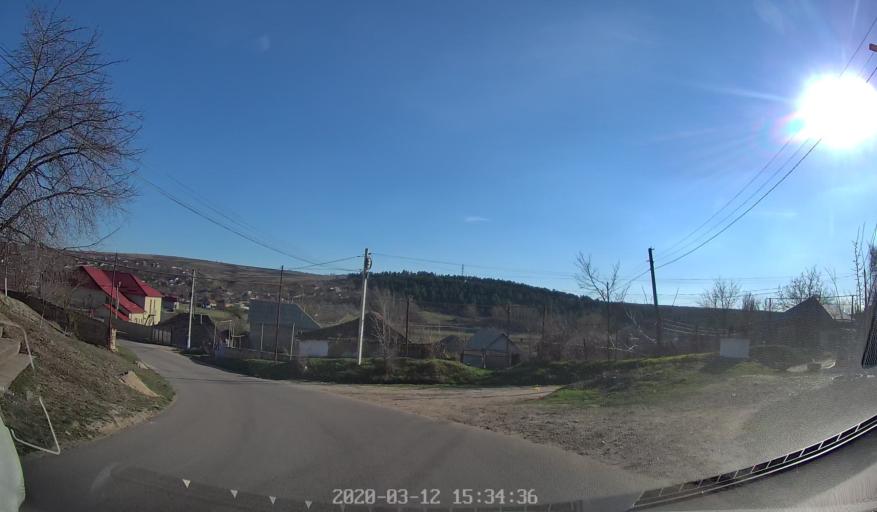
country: MD
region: Chisinau
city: Ciorescu
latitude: 47.1369
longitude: 28.9387
